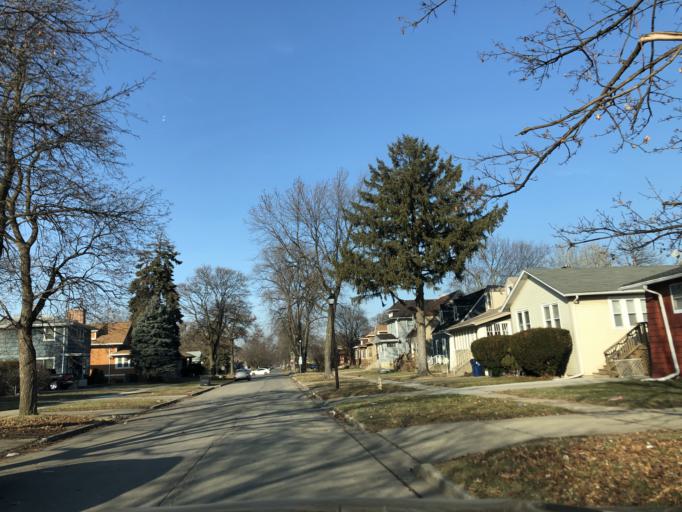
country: US
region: Illinois
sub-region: Cook County
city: Maywood
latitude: 41.8651
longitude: -87.8347
